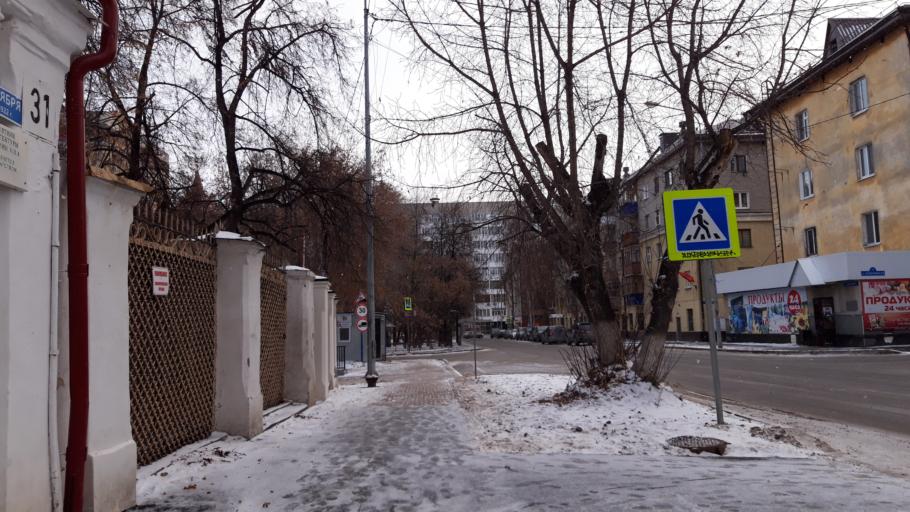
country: RU
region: Tjumen
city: Tyumen
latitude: 57.1603
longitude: 65.5497
